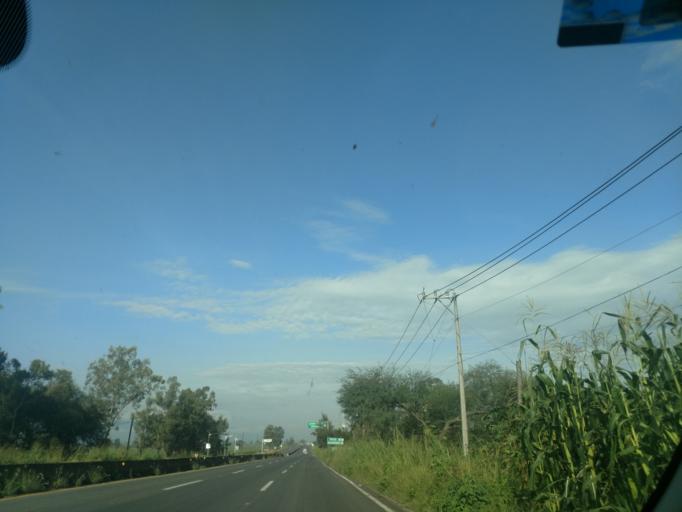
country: MX
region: Jalisco
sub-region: Ameca
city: Los Pocitos
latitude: 20.5363
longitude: -103.9448
